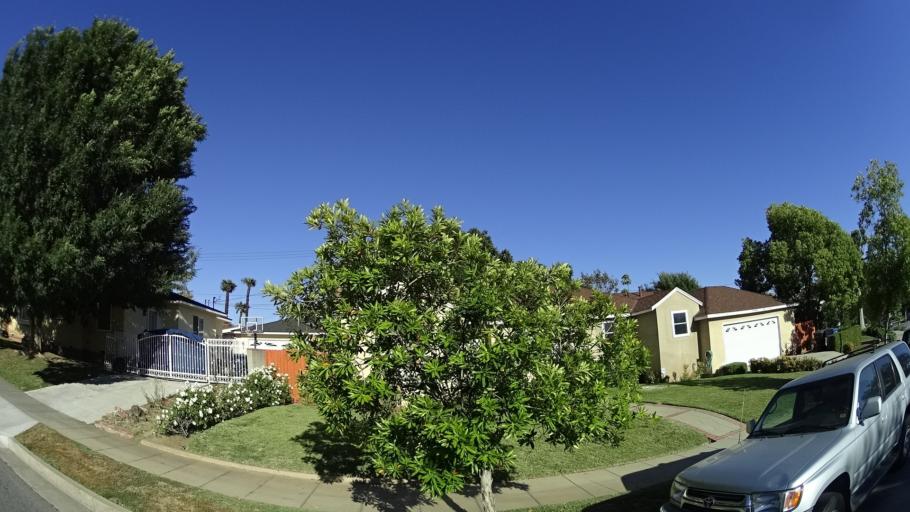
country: US
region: California
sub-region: Los Angeles County
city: Belvedere
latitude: 34.0664
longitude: -118.1598
